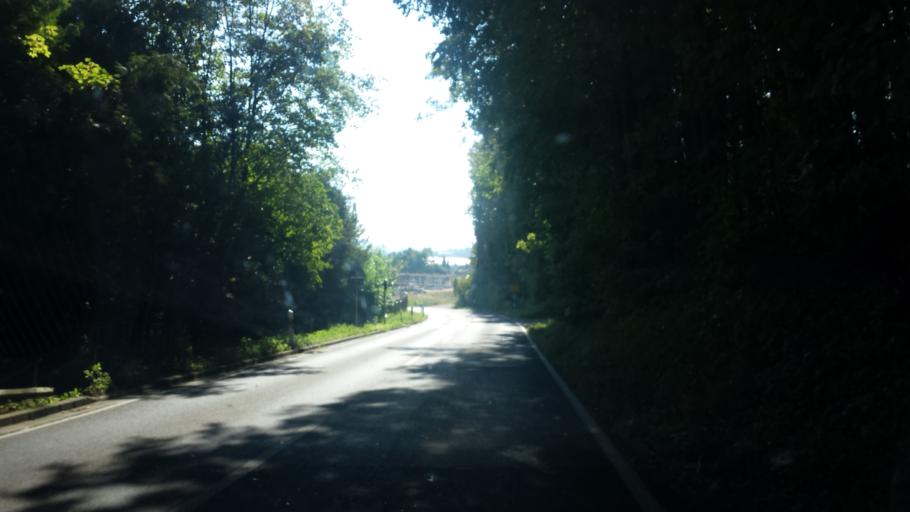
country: DE
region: Bavaria
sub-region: Lower Bavaria
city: Kelheim
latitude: 48.9118
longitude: 11.8661
